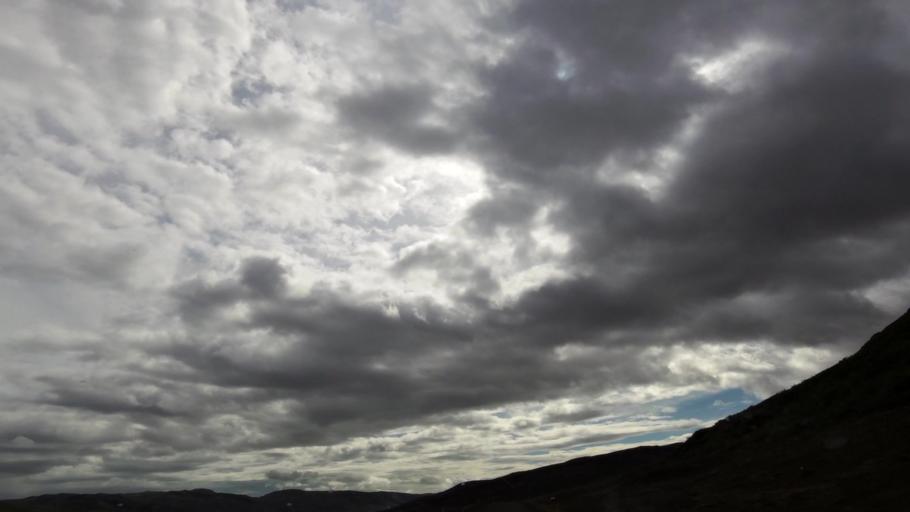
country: IS
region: West
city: Stykkisholmur
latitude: 65.5931
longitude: -22.1297
